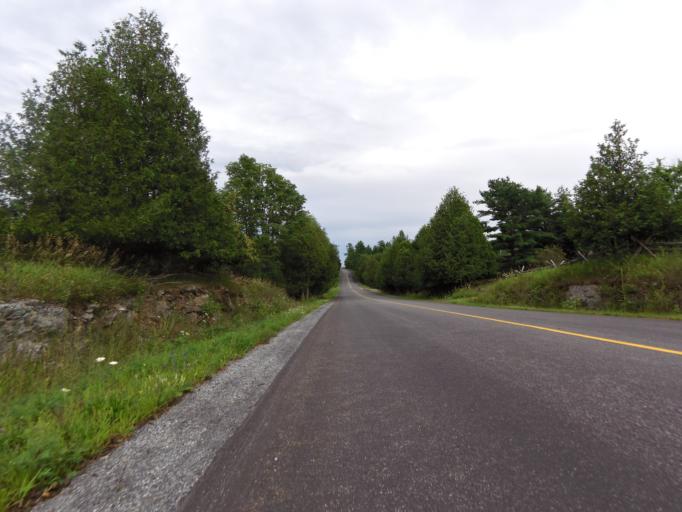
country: CA
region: Ontario
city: Perth
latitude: 45.0770
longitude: -76.3935
